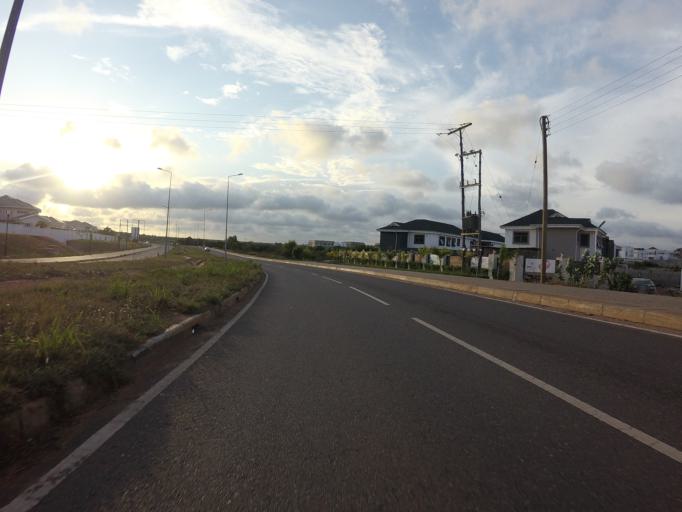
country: GH
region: Greater Accra
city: Teshi Old Town
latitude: 5.6098
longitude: -0.1414
